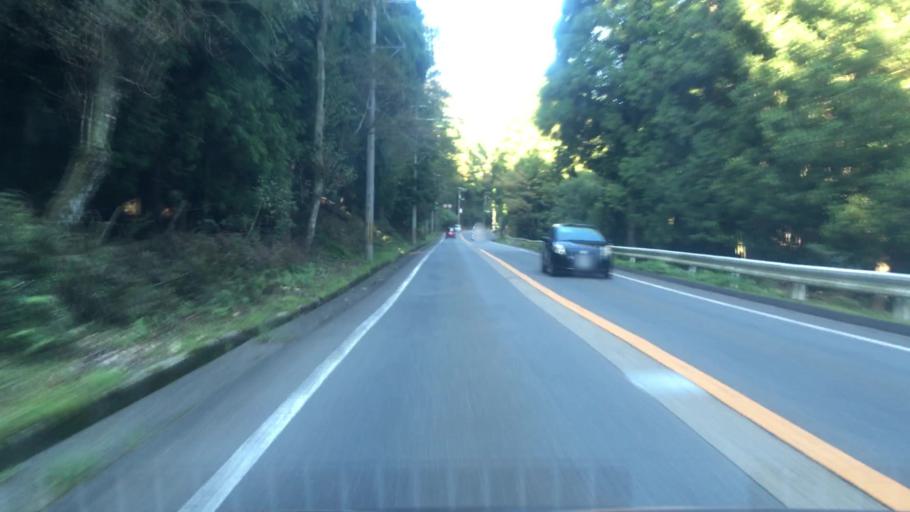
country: JP
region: Hyogo
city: Toyooka
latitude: 35.5789
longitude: 134.8561
